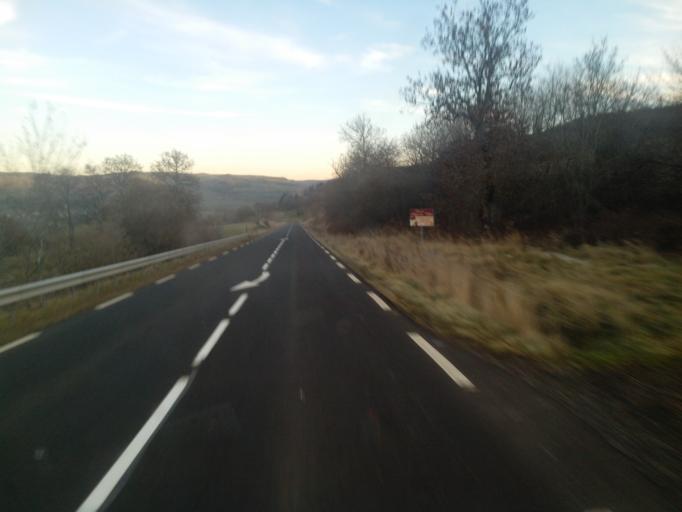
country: FR
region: Auvergne
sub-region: Departement du Cantal
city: Condat
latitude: 45.2290
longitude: 2.8004
